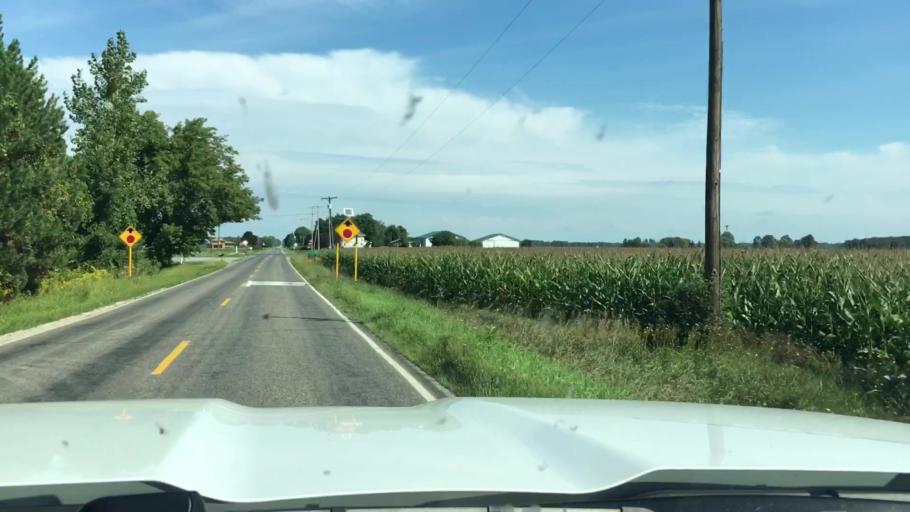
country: US
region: Michigan
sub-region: Midland County
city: Midland
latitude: 43.5231
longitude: -84.2294
